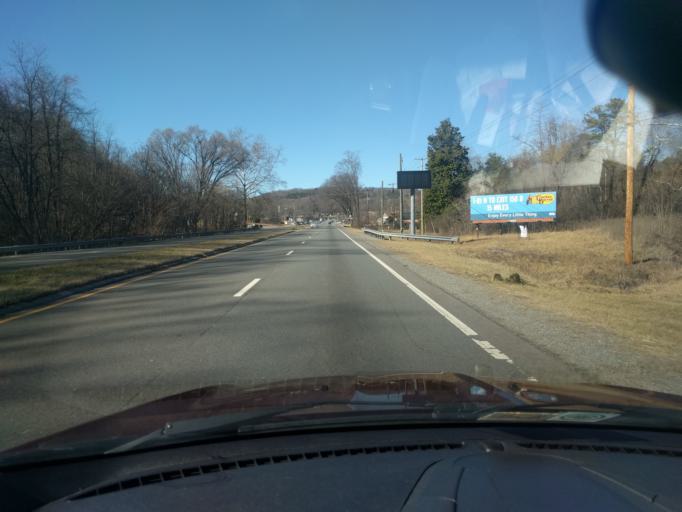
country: US
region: Virginia
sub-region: Roanoke County
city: Narrows
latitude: 37.2009
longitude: -79.9460
